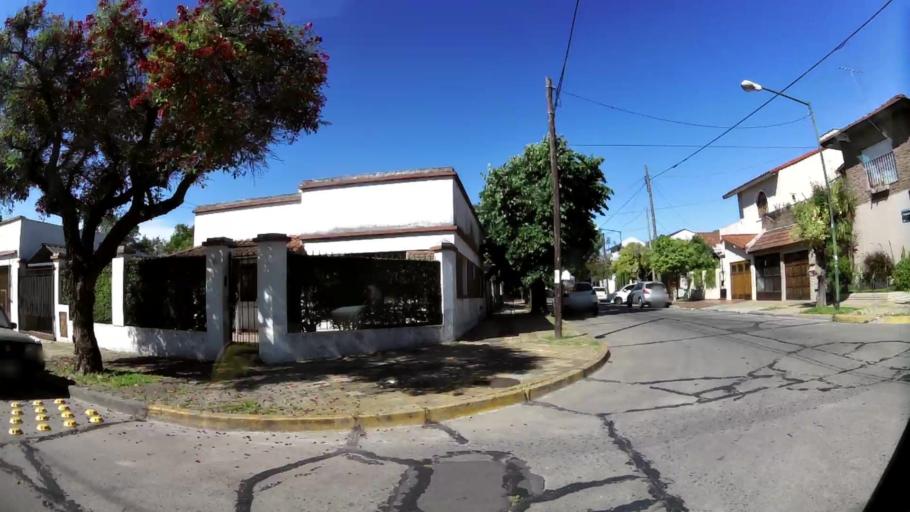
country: AR
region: Buenos Aires
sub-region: Partido de San Isidro
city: San Isidro
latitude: -34.4694
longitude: -58.5292
